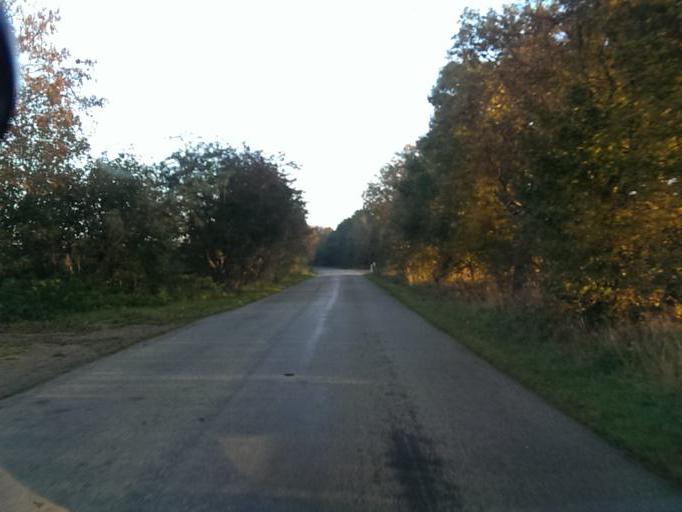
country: DK
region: South Denmark
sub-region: Esbjerg Kommune
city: Tjaereborg
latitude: 55.4697
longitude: 8.6311
